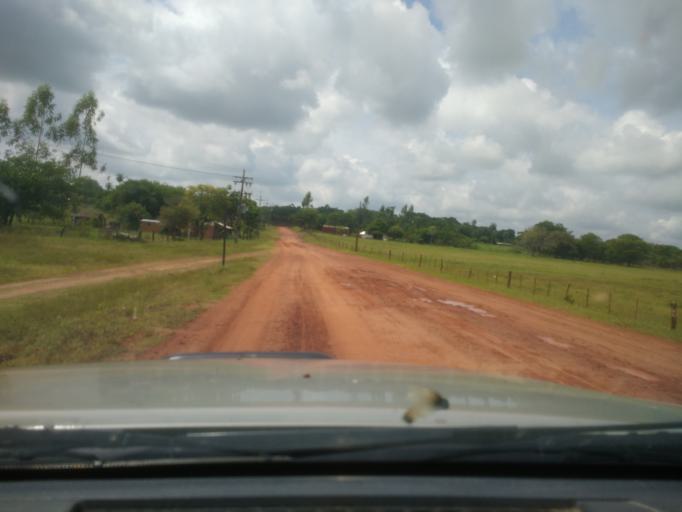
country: PY
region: San Pedro
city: Puerto Rosario
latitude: -24.4088
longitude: -57.1034
